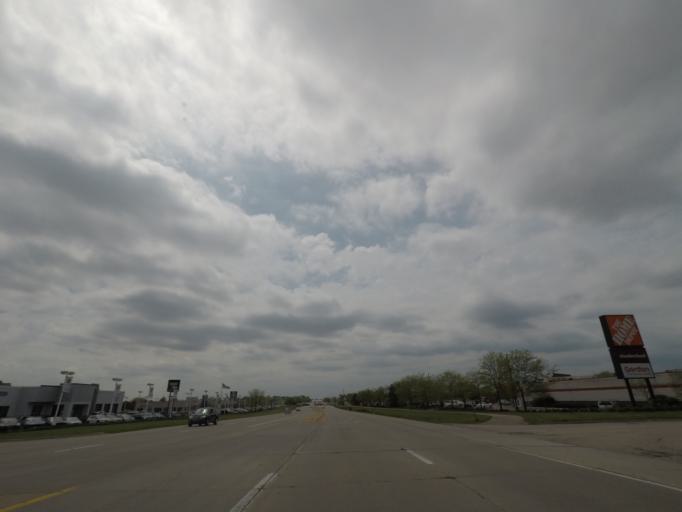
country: US
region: Illinois
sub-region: Winnebago County
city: Cherry Valley
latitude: 42.2754
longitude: -88.9800
